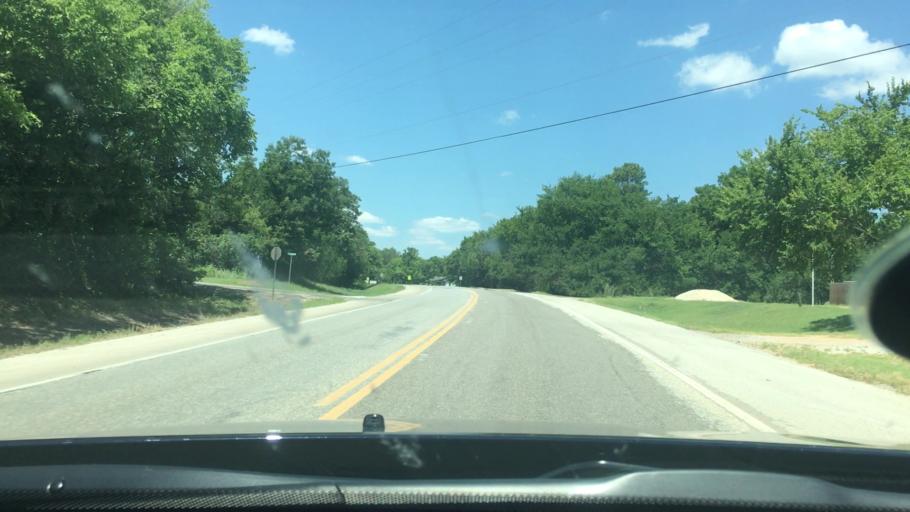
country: US
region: Oklahoma
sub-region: Carter County
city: Dickson
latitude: 34.1851
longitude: -96.8727
